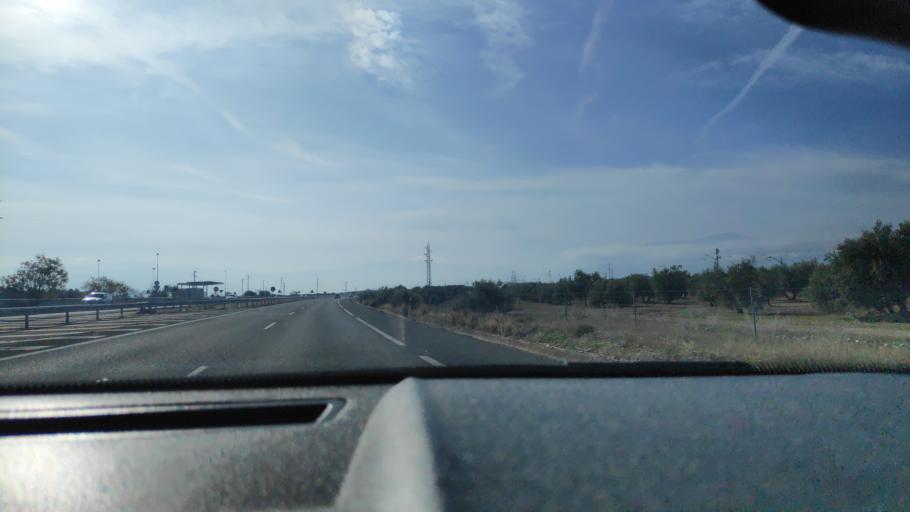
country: ES
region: Andalusia
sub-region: Provincia de Jaen
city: Jaen
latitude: 37.8447
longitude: -3.7637
